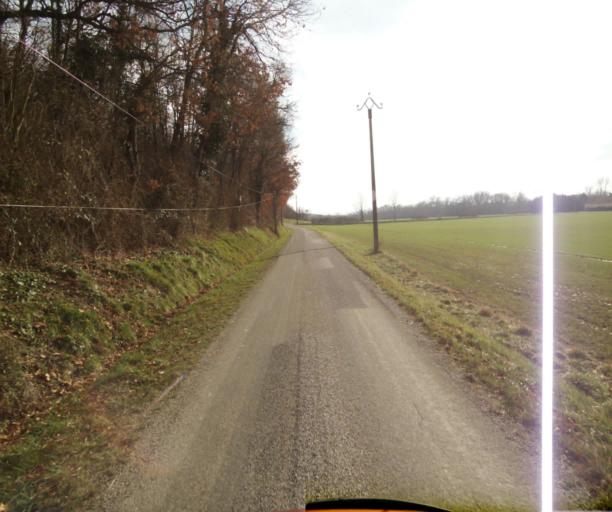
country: FR
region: Languedoc-Roussillon
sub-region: Departement de l'Aude
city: Belpech
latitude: 43.1714
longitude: 1.7378
